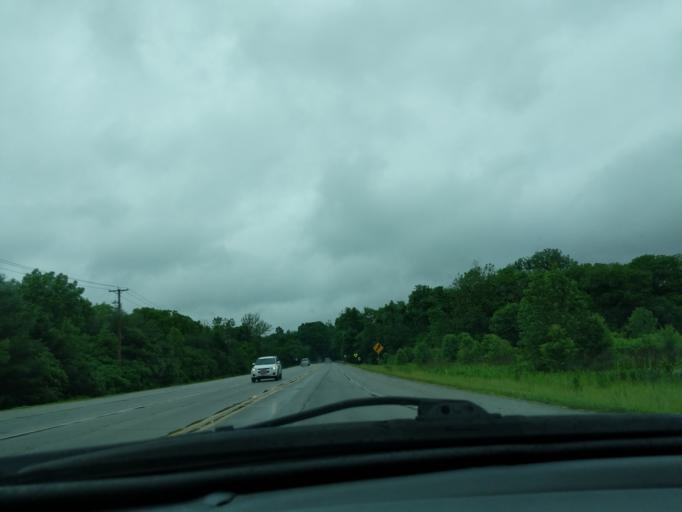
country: US
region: Indiana
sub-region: Hamilton County
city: Noblesville
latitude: 40.0552
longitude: -86.0386
